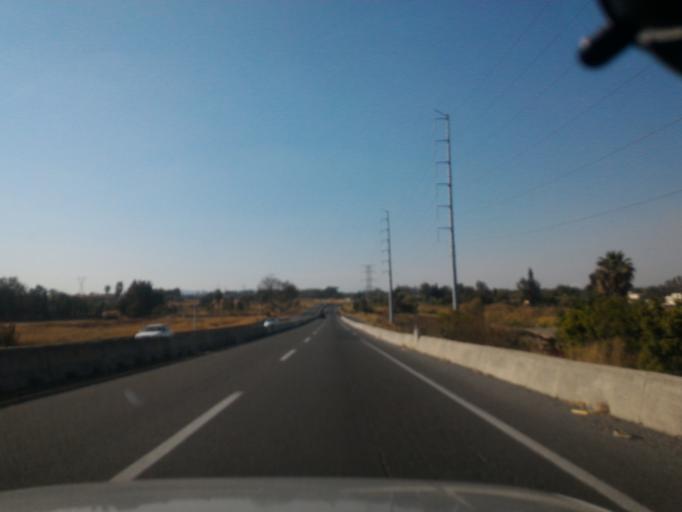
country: MX
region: Jalisco
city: Atequiza
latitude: 20.3945
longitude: -103.1431
